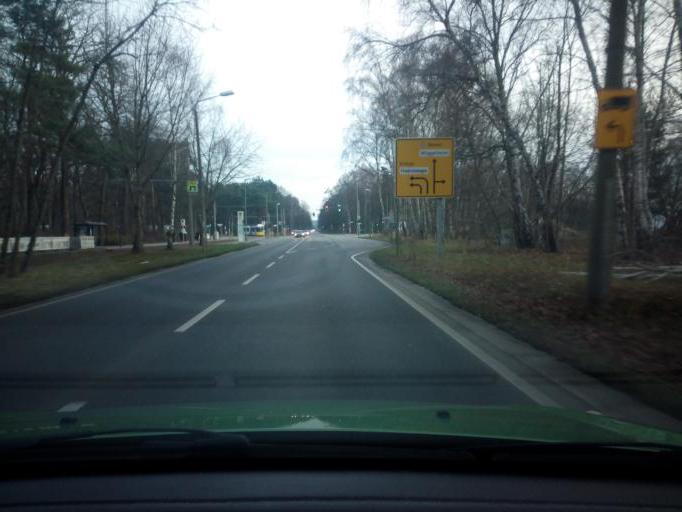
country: DE
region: Berlin
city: Berlin Koepenick
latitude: 52.4393
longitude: 13.5905
